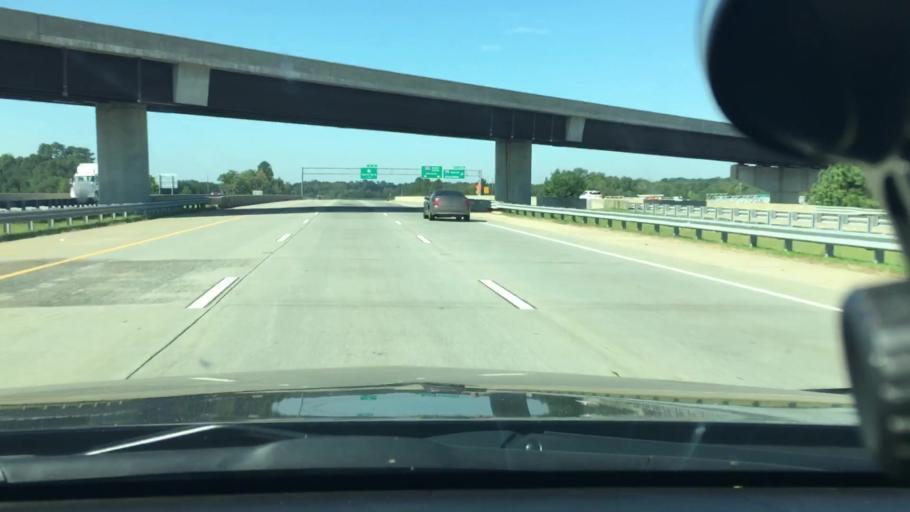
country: US
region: North Carolina
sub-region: Mecklenburg County
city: Huntersville
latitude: 35.3640
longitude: -80.8410
